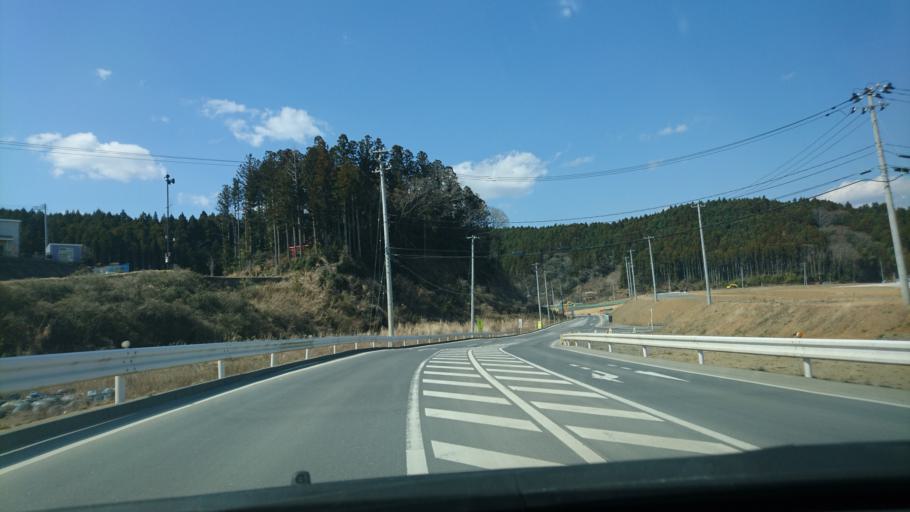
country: JP
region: Miyagi
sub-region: Oshika Gun
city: Onagawa Cho
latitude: 38.6442
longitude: 141.4378
